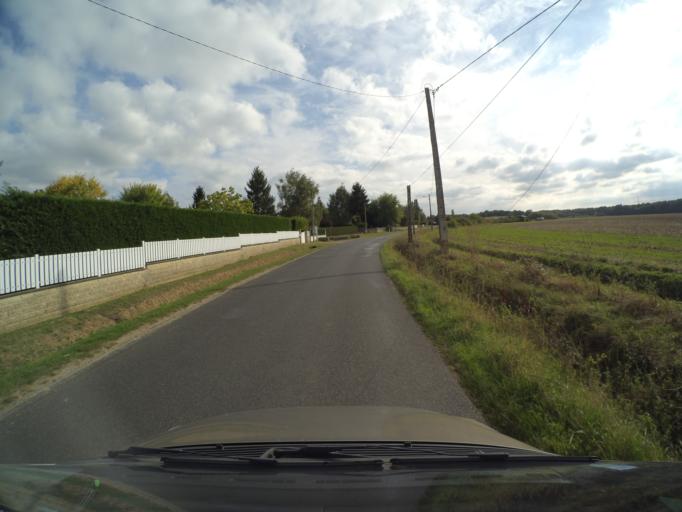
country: FR
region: Centre
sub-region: Departement d'Indre-et-Loire
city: Nazelles-Negron
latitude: 47.4734
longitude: 0.9539
